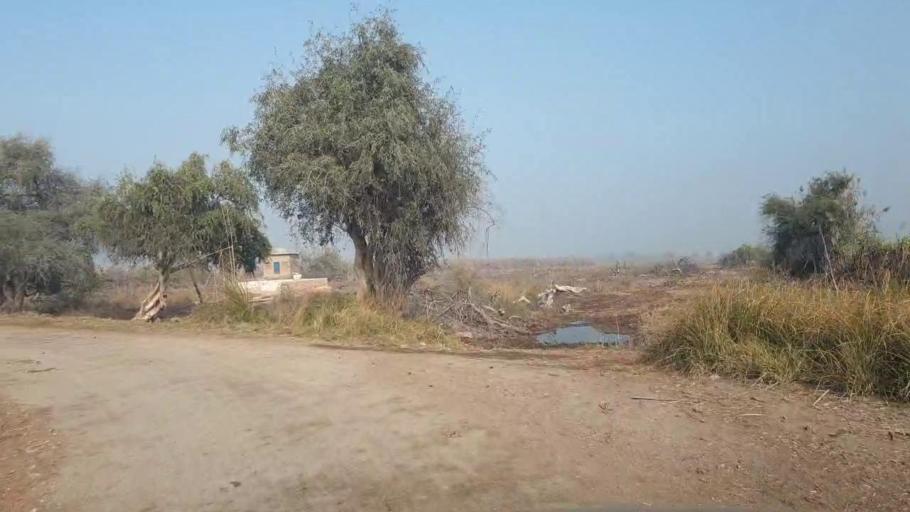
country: PK
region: Sindh
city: Shahdadpur
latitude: 25.9450
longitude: 68.5864
